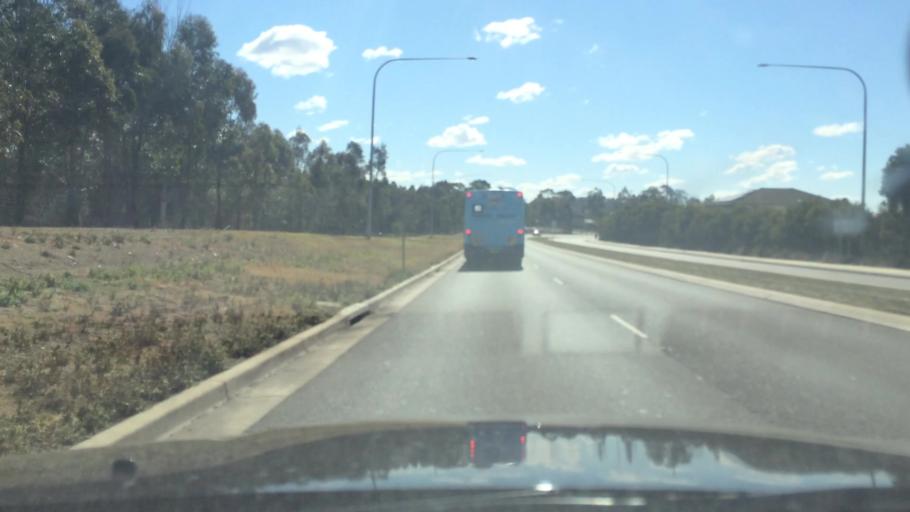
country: AU
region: New South Wales
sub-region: Campbelltown Municipality
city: Denham Court
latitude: -33.9471
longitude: 150.8378
